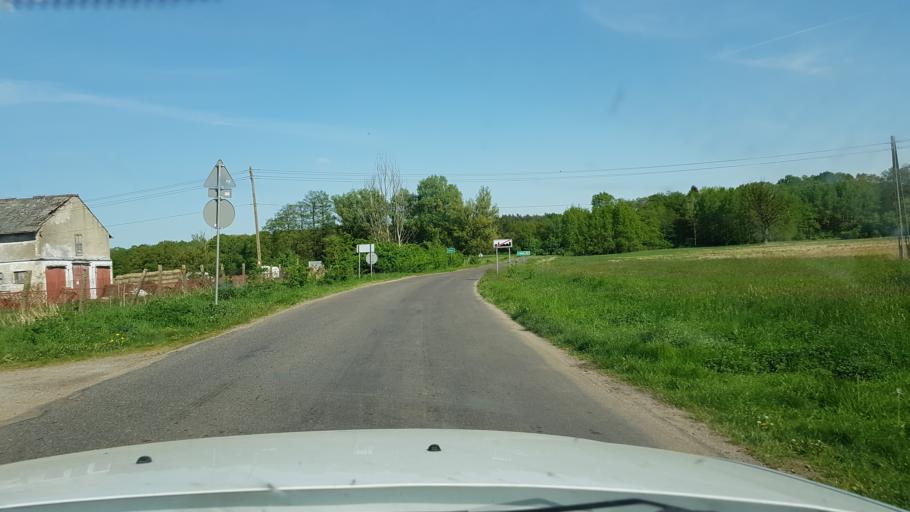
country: PL
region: West Pomeranian Voivodeship
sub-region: Powiat lobeski
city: Resko
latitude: 53.8457
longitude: 15.3644
